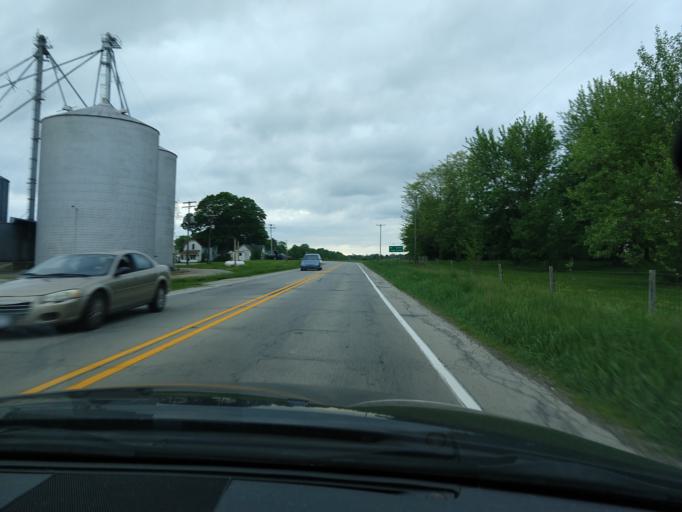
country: US
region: Indiana
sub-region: Madison County
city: Lapel
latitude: 40.0565
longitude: -85.9088
